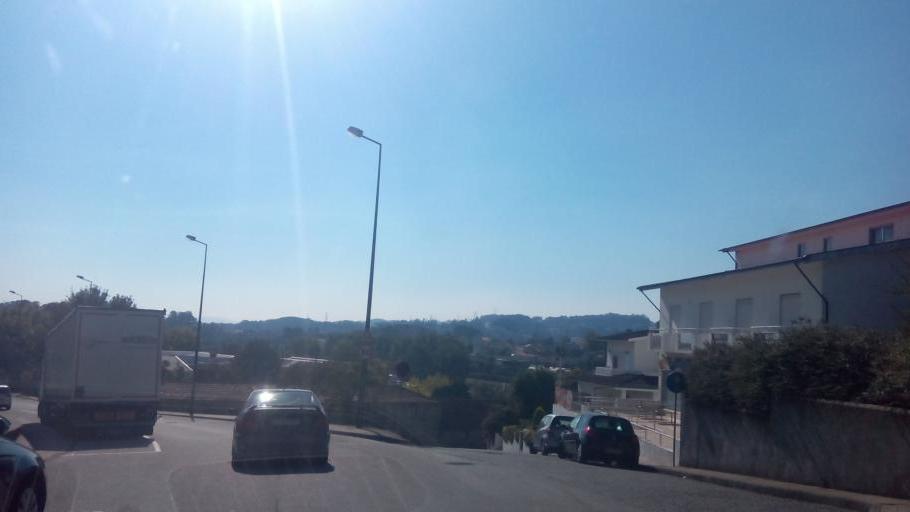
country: PT
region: Porto
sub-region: Paredes
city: Paredes
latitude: 41.2047
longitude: -8.3339
